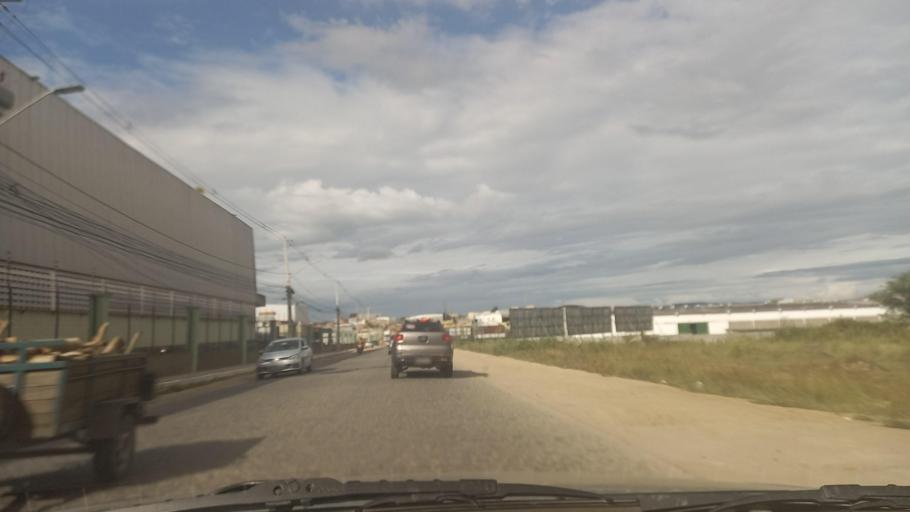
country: BR
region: Pernambuco
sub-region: Caruaru
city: Caruaru
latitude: -8.2888
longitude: -36.0115
